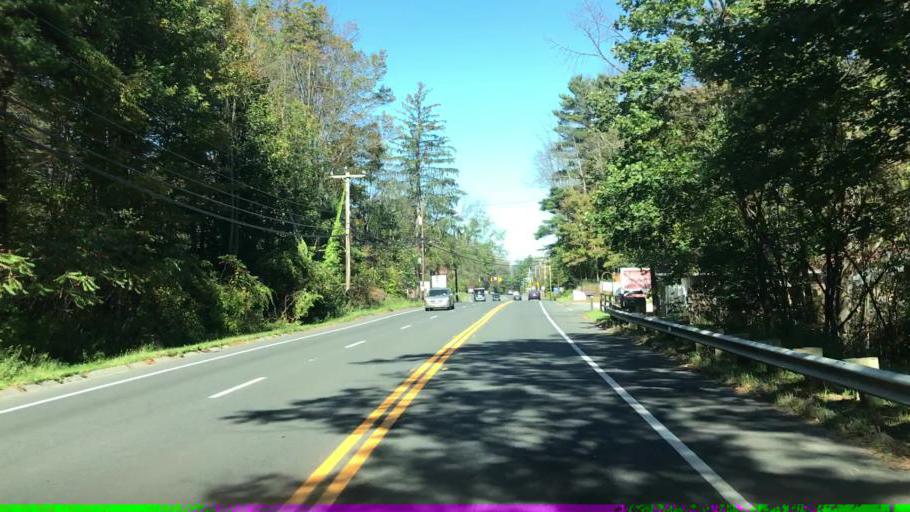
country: US
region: Massachusetts
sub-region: Berkshire County
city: Pittsfield
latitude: 42.4141
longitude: -73.2614
